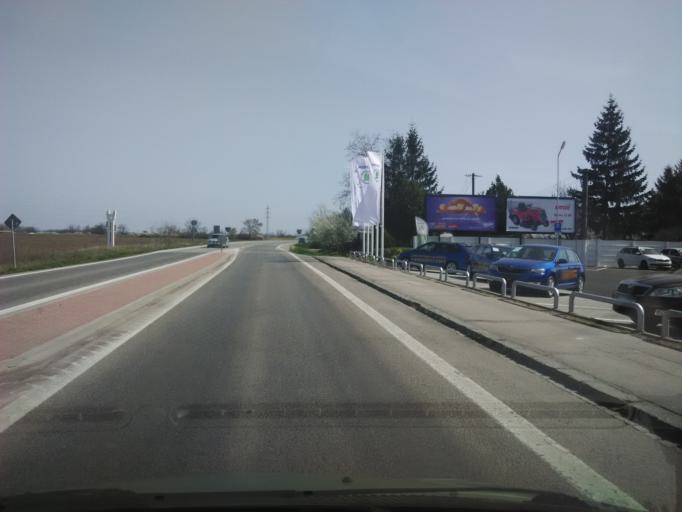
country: SK
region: Trnavsky
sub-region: Okres Galanta
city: Galanta
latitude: 48.1931
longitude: 17.7438
